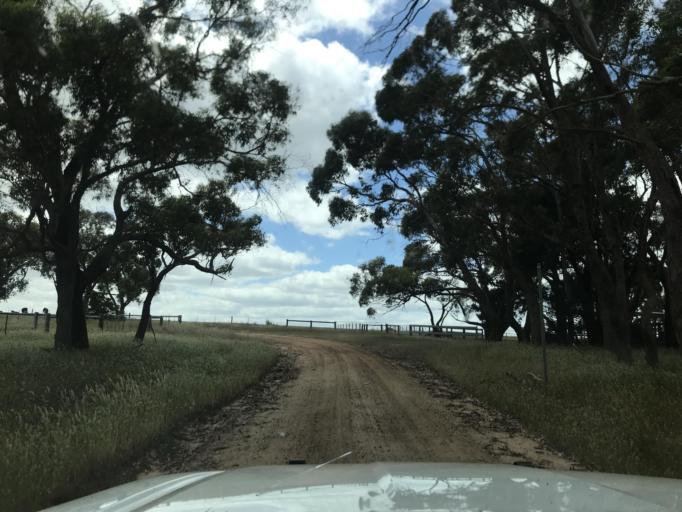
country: AU
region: South Australia
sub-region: Wattle Range
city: Penola
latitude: -37.3669
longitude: 141.2559
